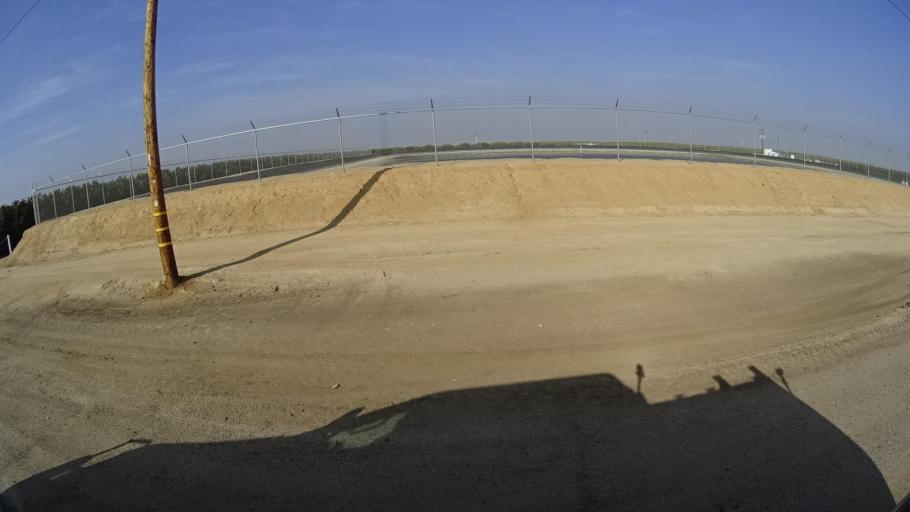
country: US
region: California
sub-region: Tulare County
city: Richgrove
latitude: 35.7908
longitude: -119.0811
